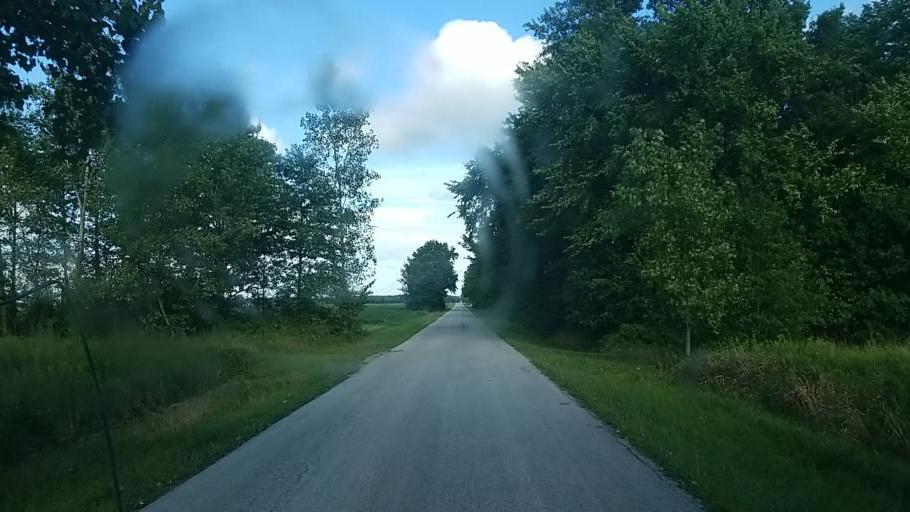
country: US
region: Ohio
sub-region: Hardin County
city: Forest
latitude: 40.7597
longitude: -83.4923
